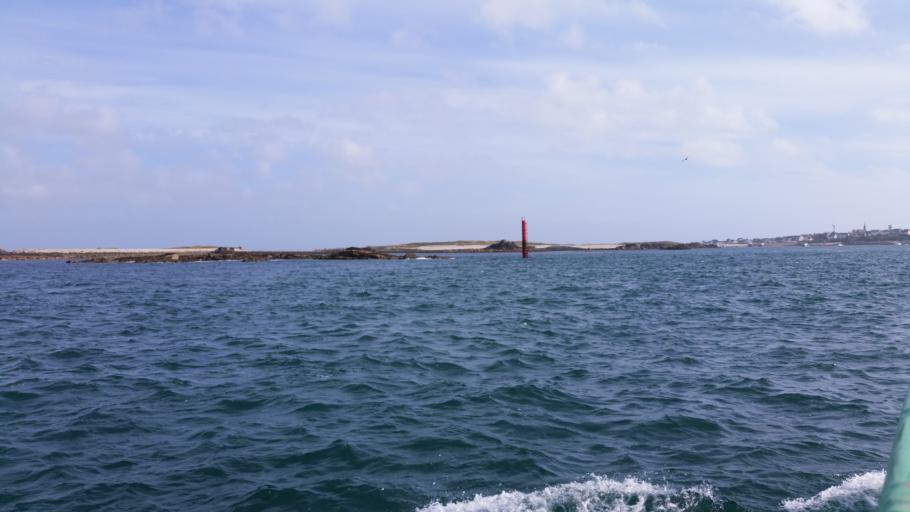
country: FR
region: Brittany
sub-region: Departement du Finistere
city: Le Conquet
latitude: 48.4107
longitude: -4.9507
